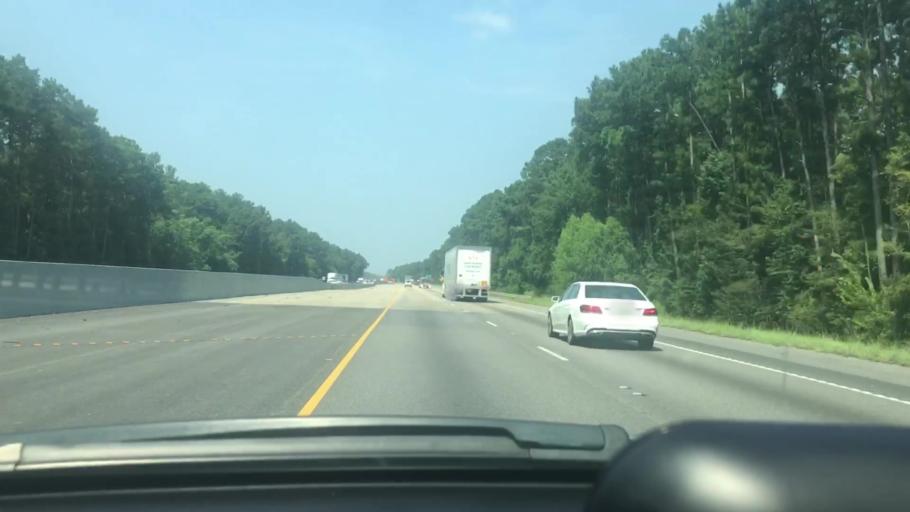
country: US
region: Louisiana
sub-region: Livingston Parish
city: Livingston
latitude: 30.4741
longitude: -90.7795
